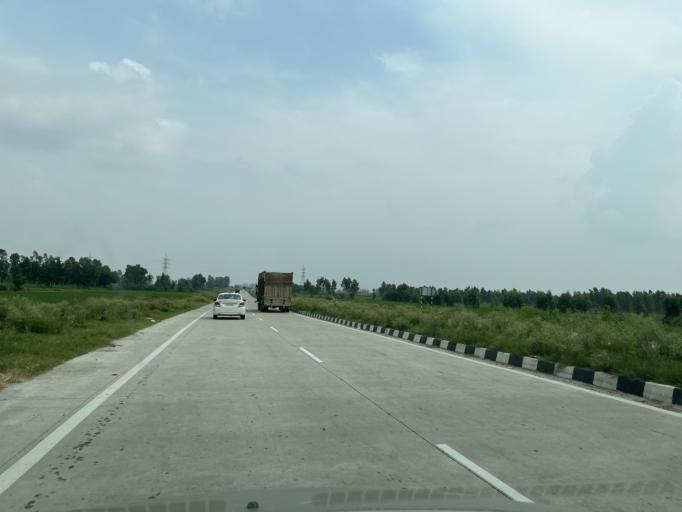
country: IN
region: Uttarakhand
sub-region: Udham Singh Nagar
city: Kashipur
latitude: 29.1707
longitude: 78.9520
